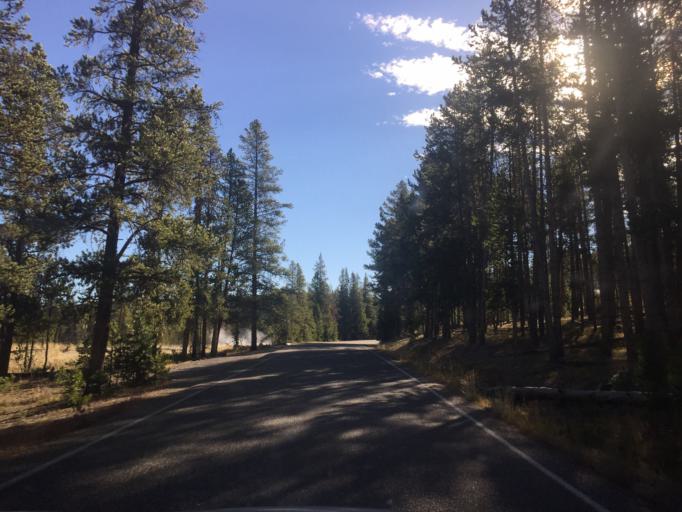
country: US
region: Montana
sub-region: Gallatin County
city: West Yellowstone
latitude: 44.5357
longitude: -110.8057
